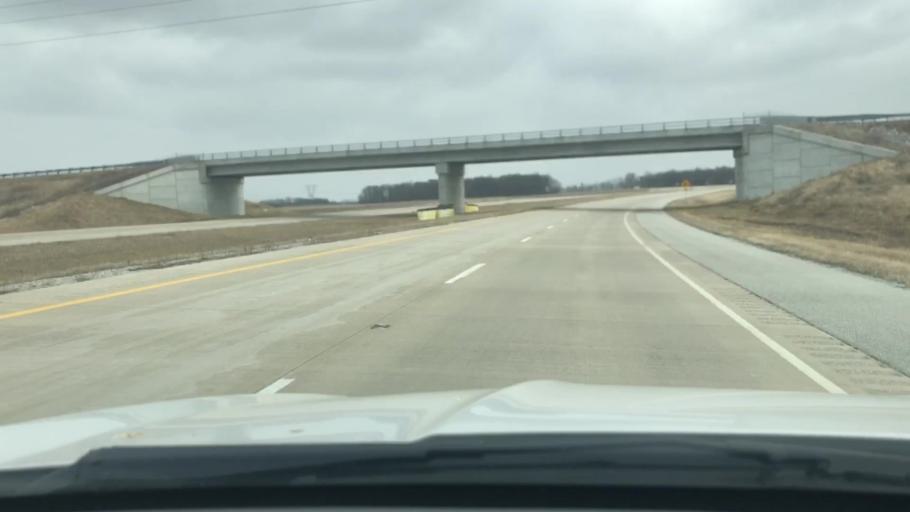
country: US
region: Indiana
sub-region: Carroll County
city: Delphi
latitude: 40.6223
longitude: -86.6215
